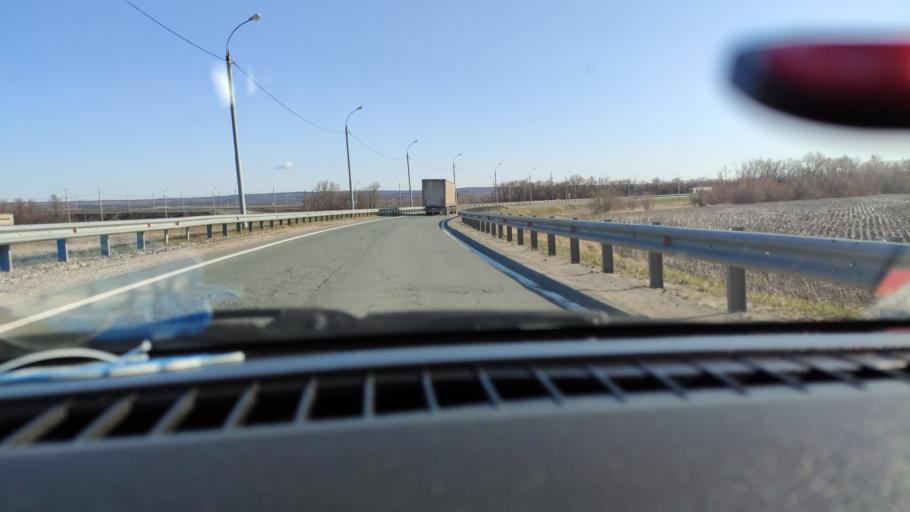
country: RU
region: Samara
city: Varlamovo
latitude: 53.1947
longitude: 48.2944
